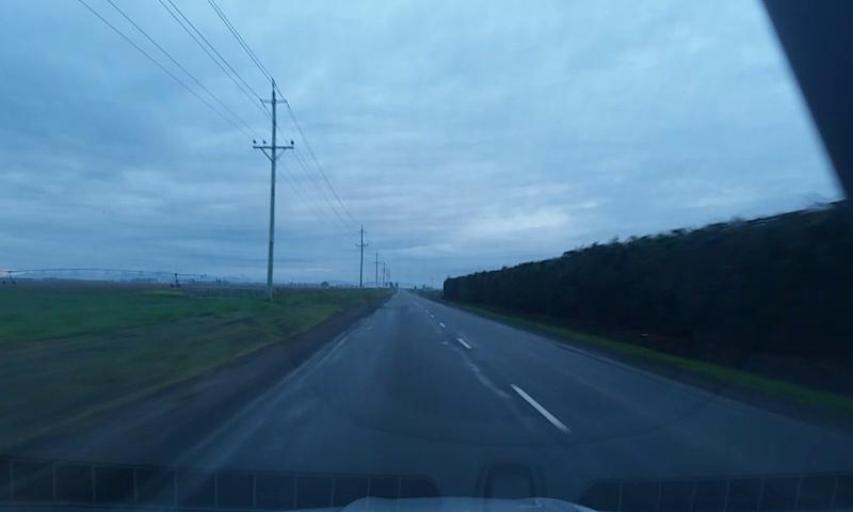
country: NZ
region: Canterbury
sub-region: Ashburton District
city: Rakaia
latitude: -43.7557
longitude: 171.9251
